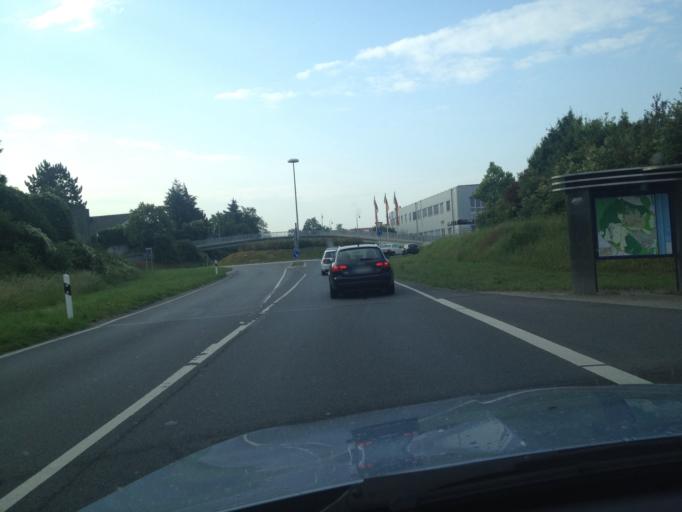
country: DE
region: Baden-Wuerttemberg
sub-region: Karlsruhe Region
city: Walldorf
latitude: 49.3094
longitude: 8.6305
